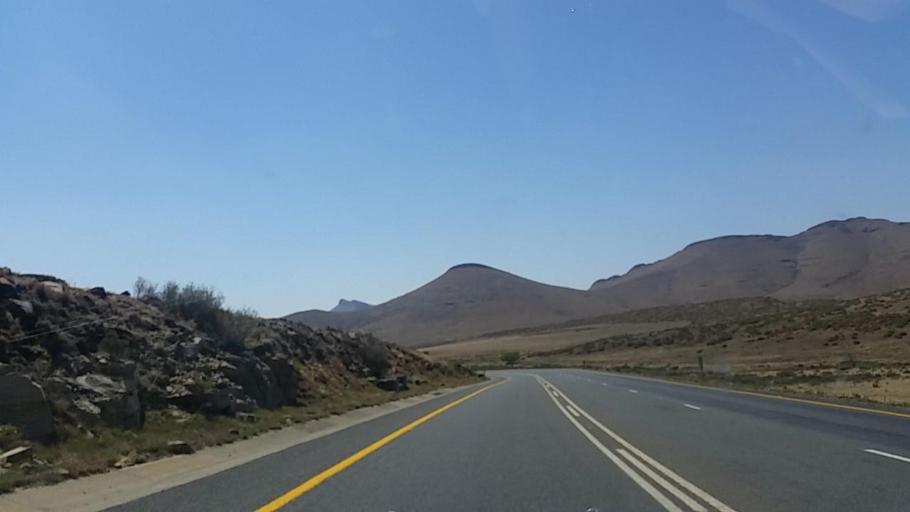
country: ZA
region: Eastern Cape
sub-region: Chris Hani District Municipality
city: Middelburg
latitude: -31.8179
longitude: 24.8617
